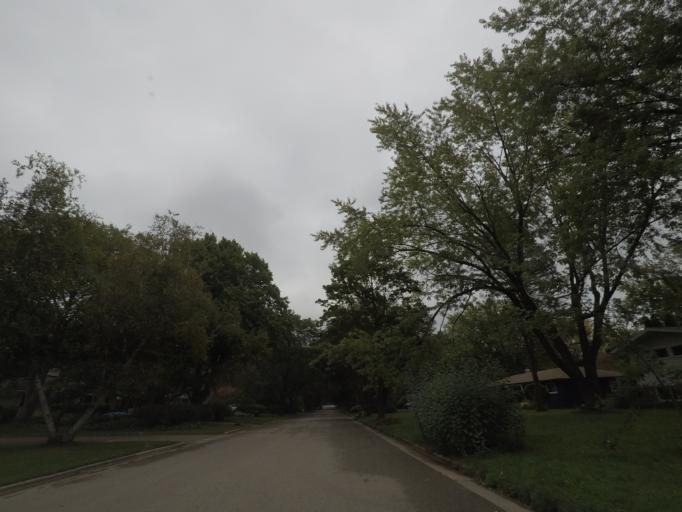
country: US
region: Wisconsin
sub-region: Dane County
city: Shorewood Hills
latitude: 43.0379
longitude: -89.4733
